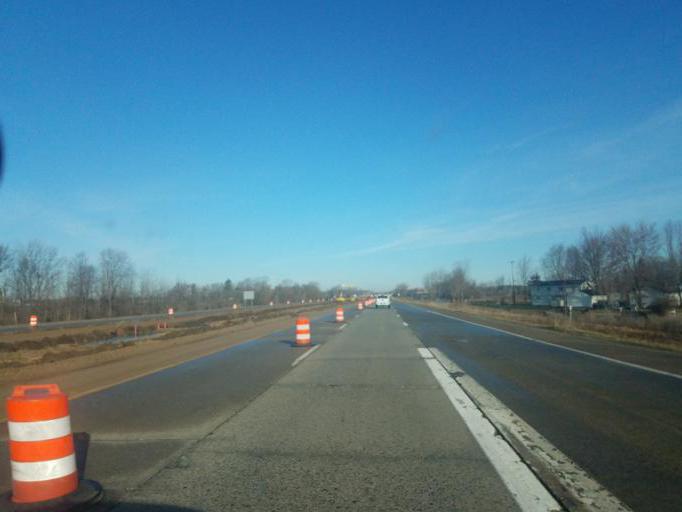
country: US
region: Michigan
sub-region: Gratiot County
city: Saint Louis
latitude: 43.3848
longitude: -84.6118
